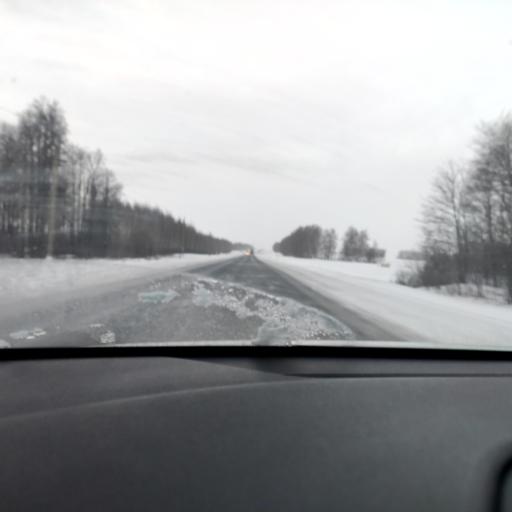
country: RU
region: Tatarstan
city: Verkhniy Uslon
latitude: 55.6465
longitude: 48.8311
